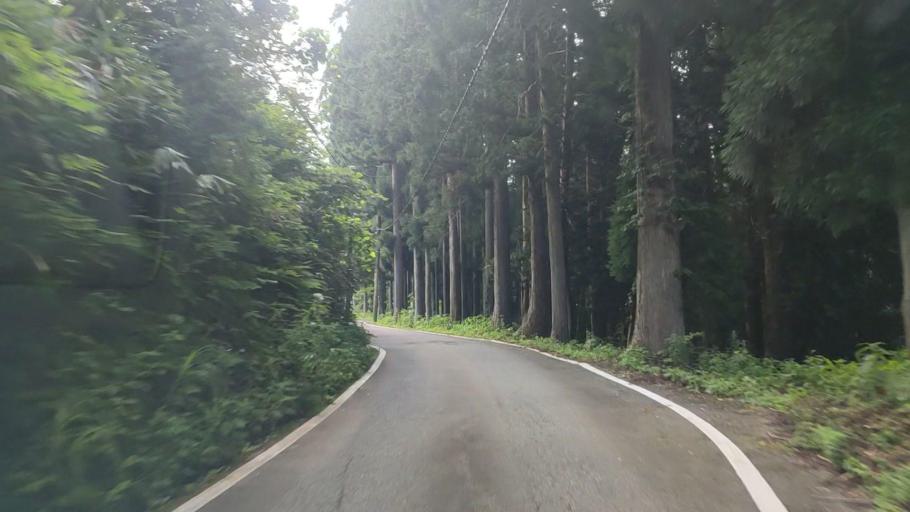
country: JP
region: Fukui
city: Katsuyama
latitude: 36.2252
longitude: 136.5306
